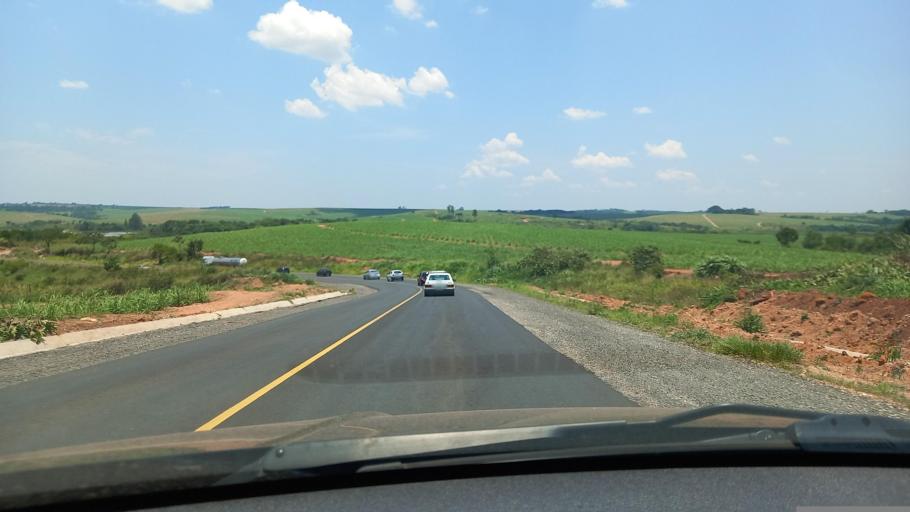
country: BR
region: Sao Paulo
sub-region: Moji-Guacu
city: Mogi-Gaucu
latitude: -22.3717
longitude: -46.8754
